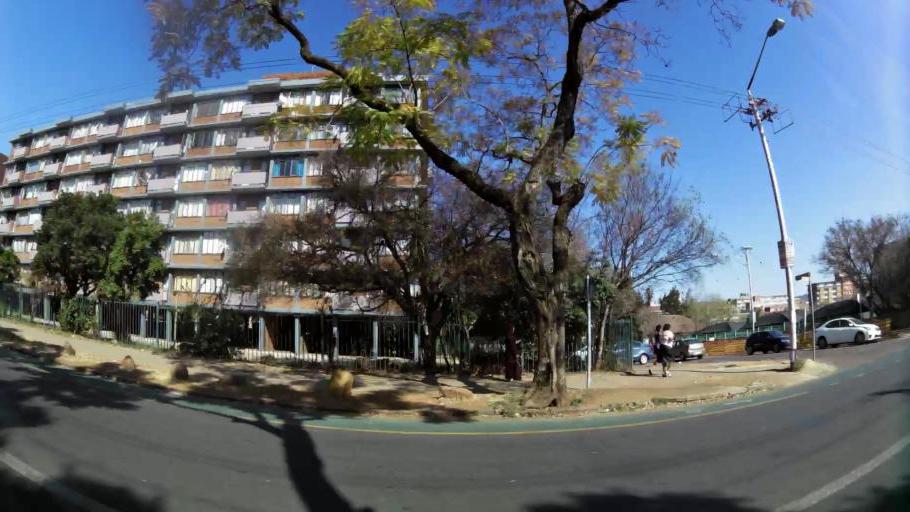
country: ZA
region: Gauteng
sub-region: City of Tshwane Metropolitan Municipality
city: Pretoria
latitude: -25.7490
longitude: 28.2081
